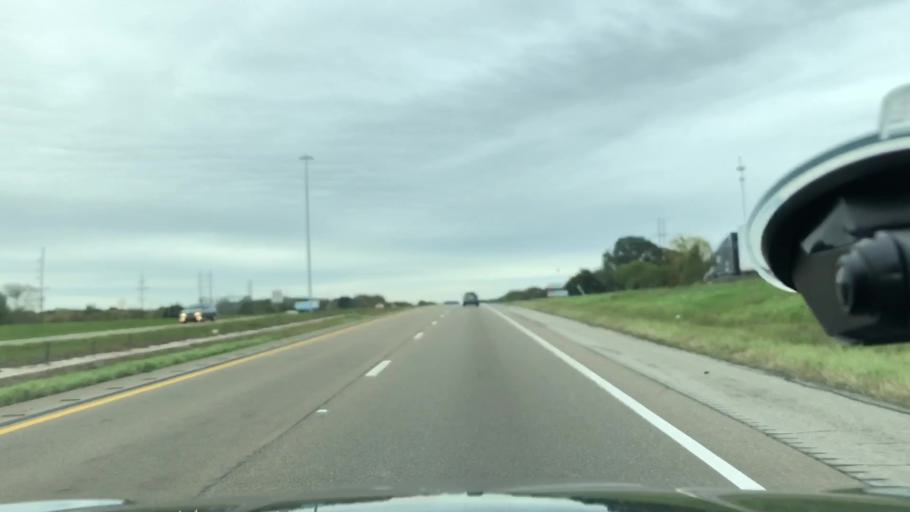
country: US
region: Texas
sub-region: Franklin County
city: Mount Vernon
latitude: 33.1600
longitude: -95.1109
